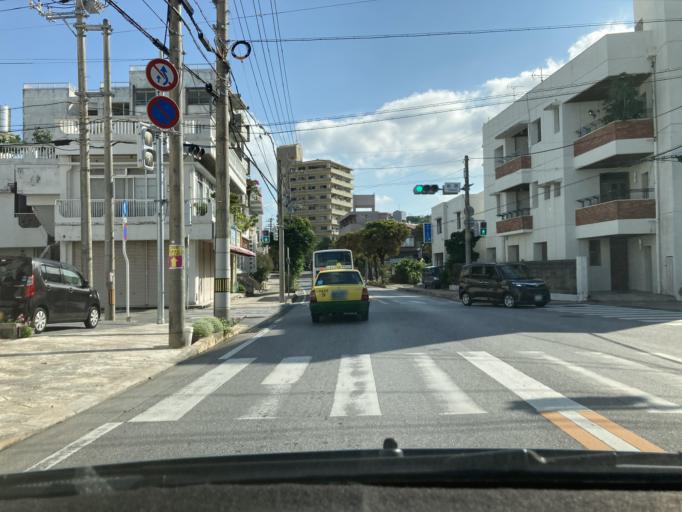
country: JP
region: Okinawa
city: Naha-shi
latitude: 26.2235
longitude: 127.7166
